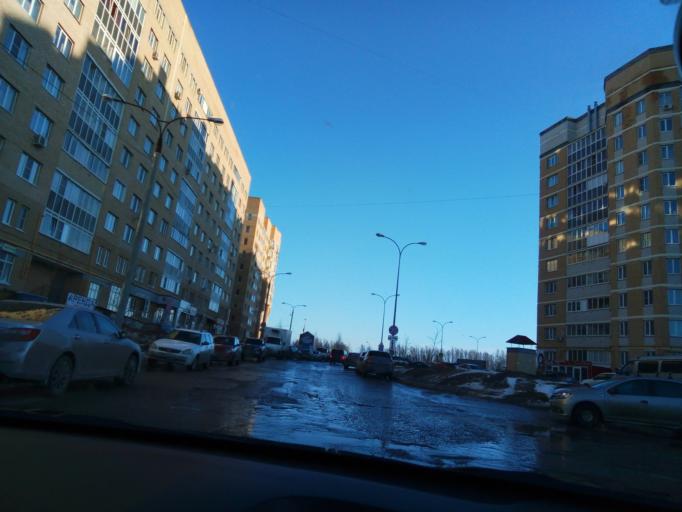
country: RU
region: Chuvashia
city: Novyye Lapsary
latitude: 56.1338
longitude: 47.1588
